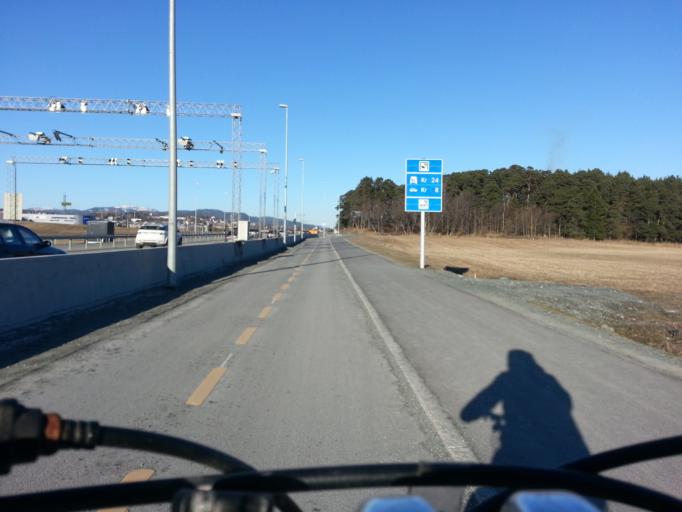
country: NO
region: Sor-Trondelag
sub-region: Trondheim
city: Trondheim
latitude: 63.4315
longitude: 10.4805
